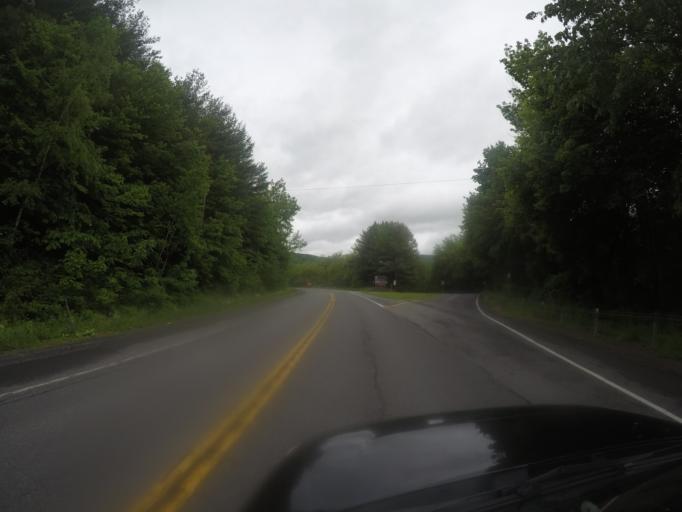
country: US
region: New York
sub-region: Ulster County
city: Shokan
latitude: 42.0791
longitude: -74.3090
